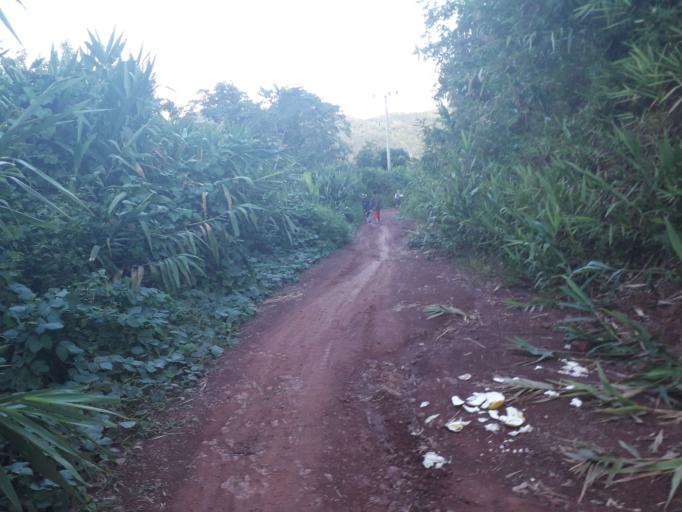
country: CN
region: Yunnan
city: Menglie
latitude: 22.1256
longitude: 101.7594
